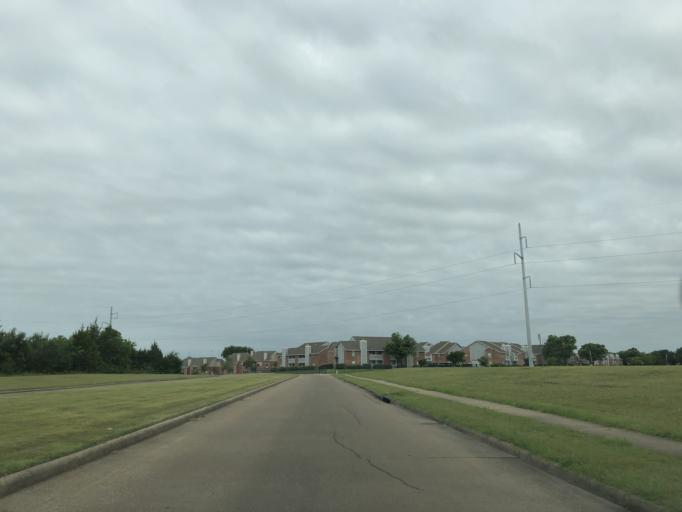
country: US
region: Texas
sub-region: Dallas County
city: Sunnyvale
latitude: 32.8411
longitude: -96.6187
